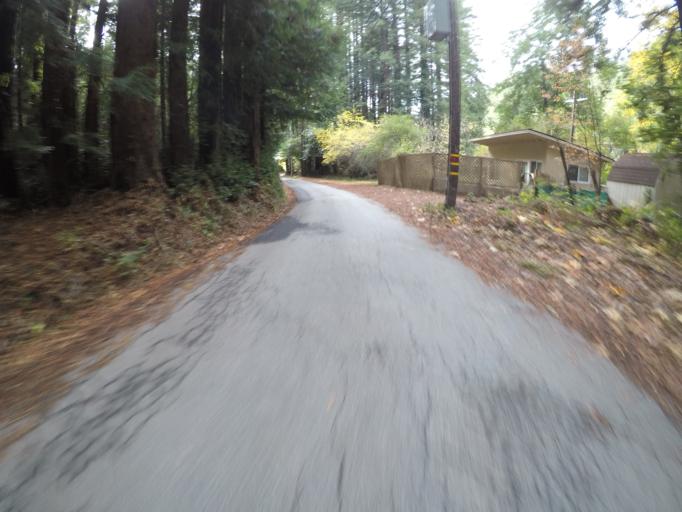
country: US
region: California
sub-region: Santa Cruz County
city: Scotts Valley
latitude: 37.0379
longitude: -121.9785
